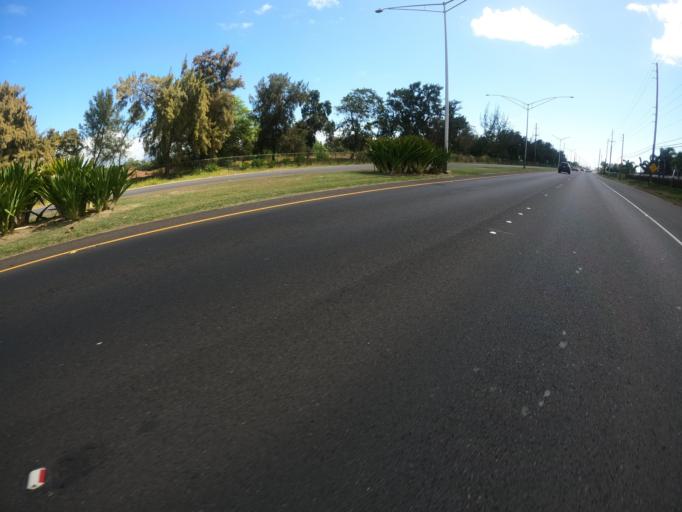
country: US
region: Hawaii
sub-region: Honolulu County
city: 'Ewa Beach
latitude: 21.3263
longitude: -158.0190
